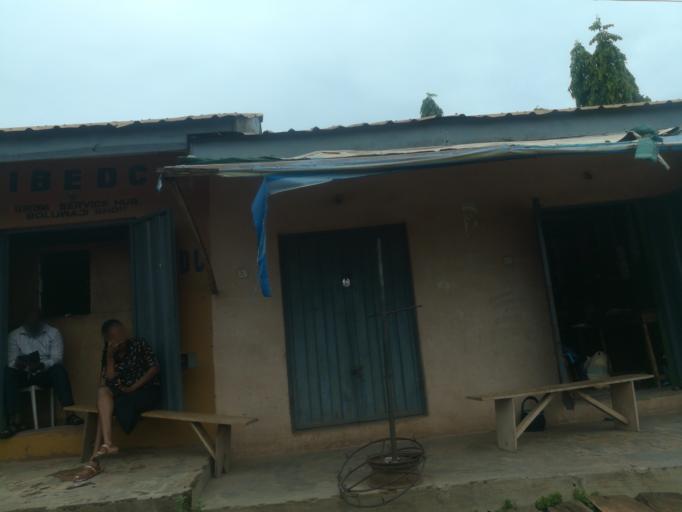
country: NG
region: Oyo
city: Ibadan
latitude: 7.3387
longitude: 3.9072
